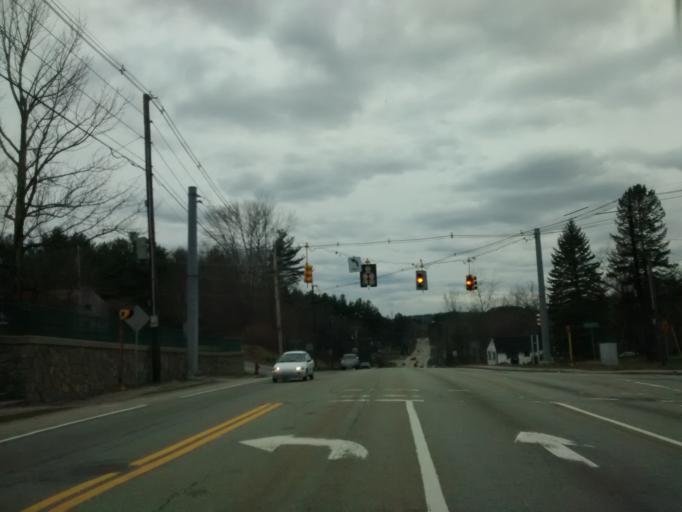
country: US
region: Massachusetts
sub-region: Worcester County
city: Charlton
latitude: 42.1452
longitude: -71.9898
